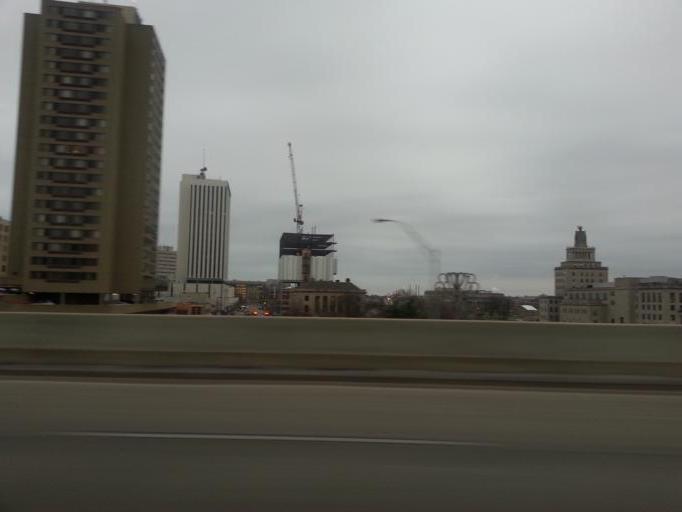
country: US
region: Iowa
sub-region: Linn County
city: Cedar Rapids
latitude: 41.9794
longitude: -91.6712
